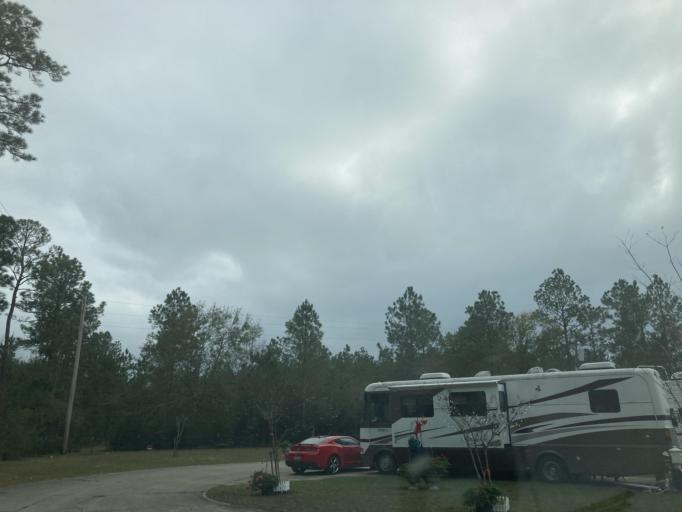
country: US
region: Mississippi
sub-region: Jackson County
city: Latimer
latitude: 30.5379
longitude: -88.9219
